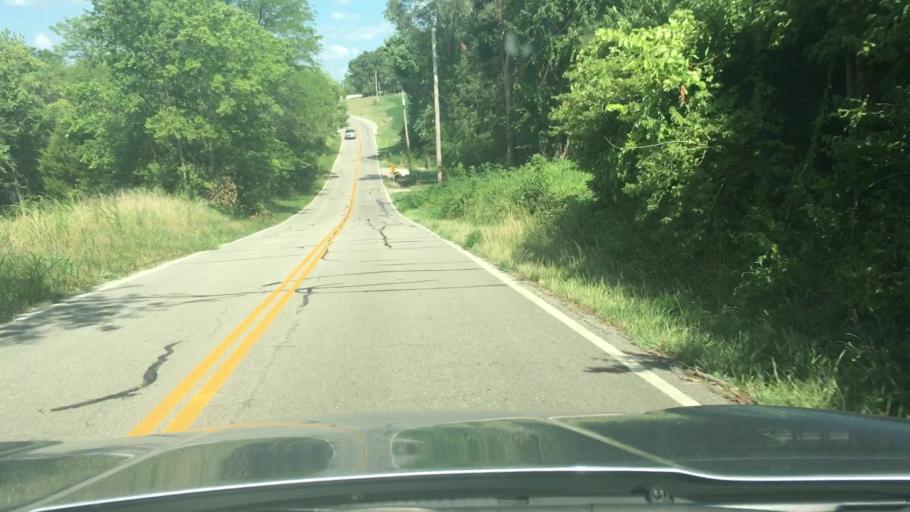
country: US
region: Missouri
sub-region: Jackson County
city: Lees Summit
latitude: 38.8896
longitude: -94.4013
